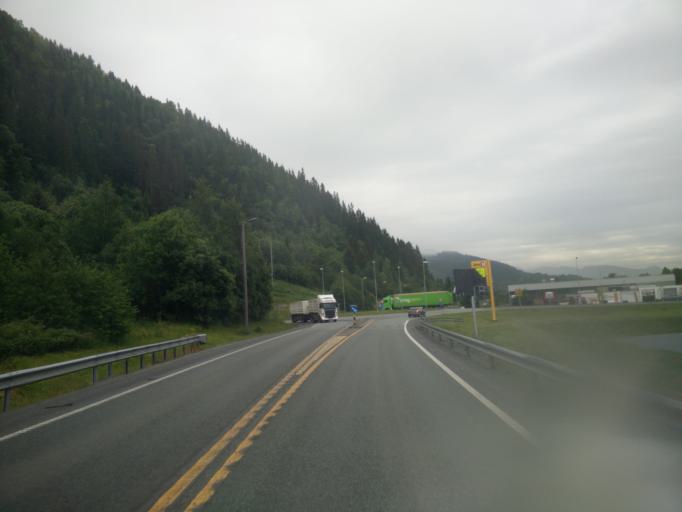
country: NO
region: Sor-Trondelag
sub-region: Orkdal
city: Orkanger
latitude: 63.2974
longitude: 9.8540
